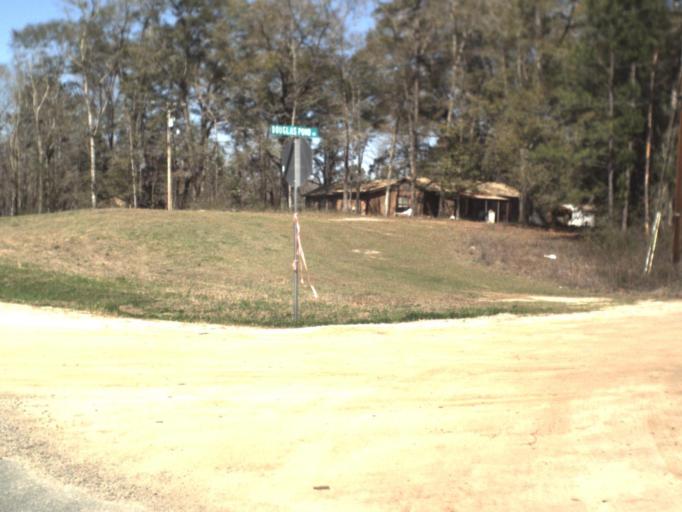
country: US
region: Florida
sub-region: Jackson County
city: Marianna
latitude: 30.7403
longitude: -85.1237
